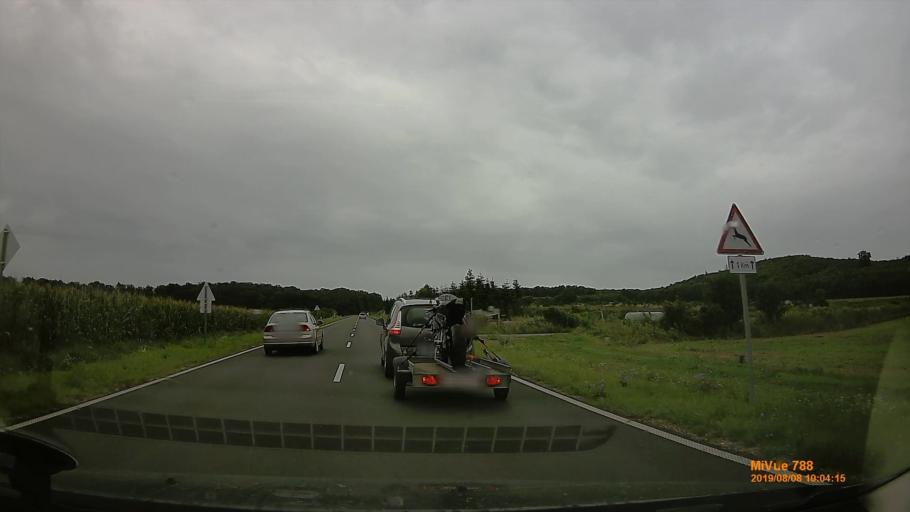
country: HU
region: Zala
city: Zalaegerszeg
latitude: 46.9178
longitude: 16.8592
